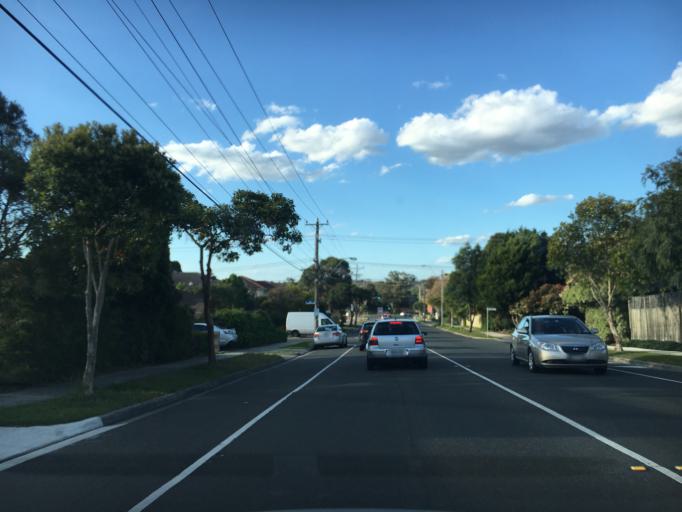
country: AU
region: Victoria
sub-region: Whitehorse
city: Vermont South
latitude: -37.8774
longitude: 145.1786
